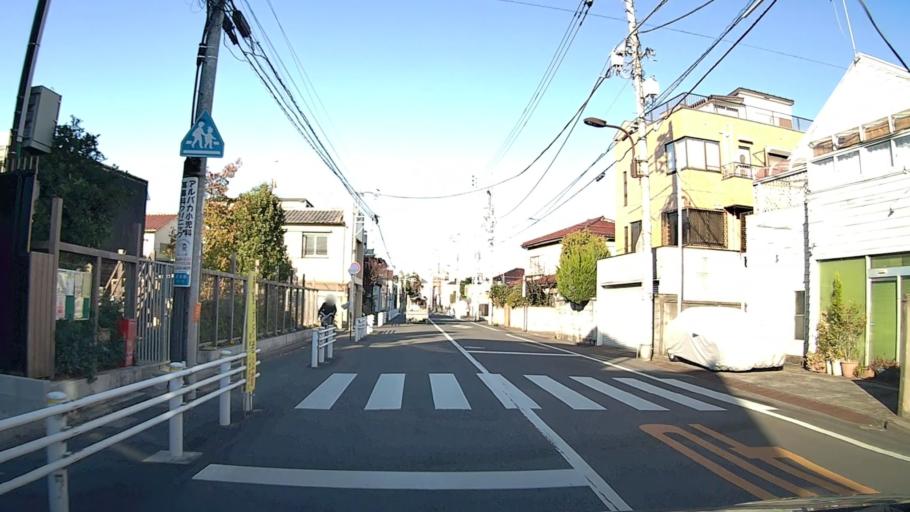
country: JP
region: Tokyo
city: Tokyo
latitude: 35.7242
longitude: 139.6754
